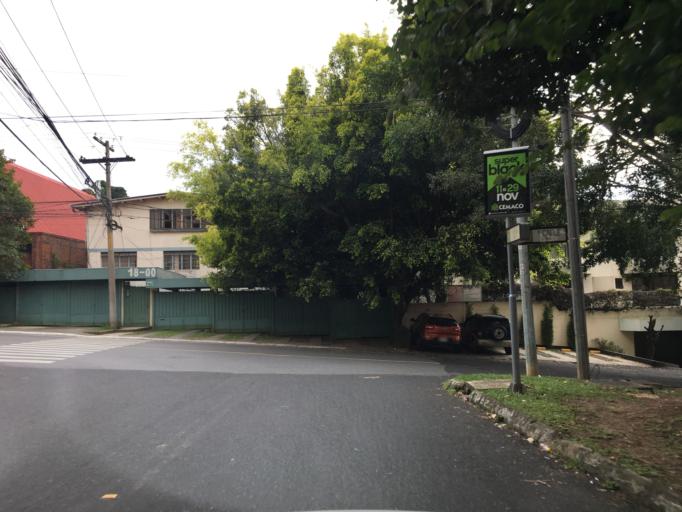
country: GT
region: Guatemala
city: Santa Catarina Pinula
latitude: 14.5938
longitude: -90.4960
